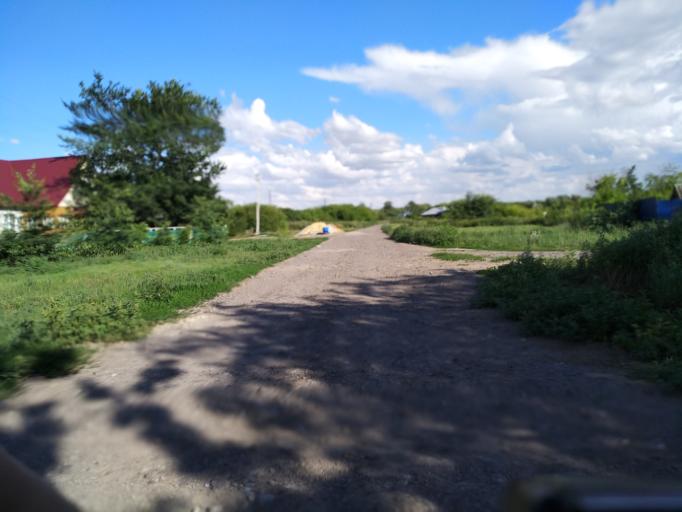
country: RU
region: Lipetsk
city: Dobrinka
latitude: 52.0341
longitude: 40.5607
